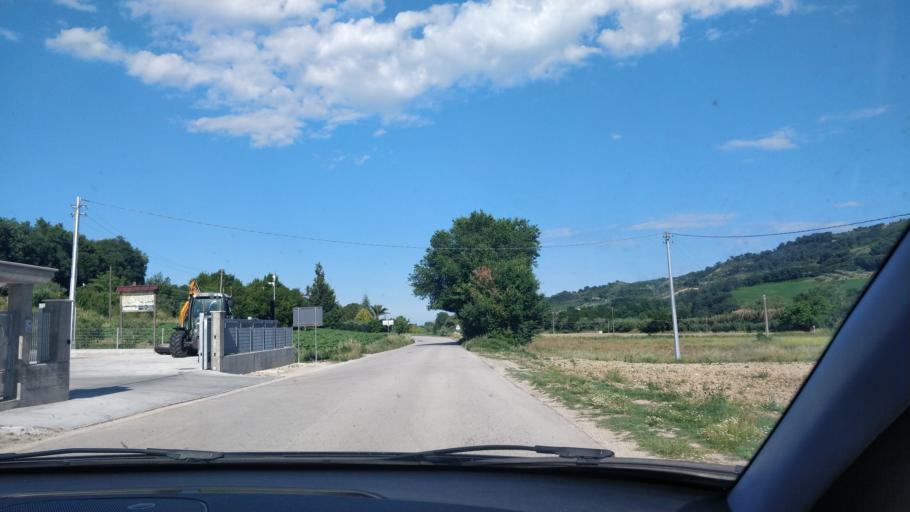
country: IT
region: The Marches
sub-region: Provincia di Ascoli Piceno
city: Massignano
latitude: 43.0371
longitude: 13.8024
